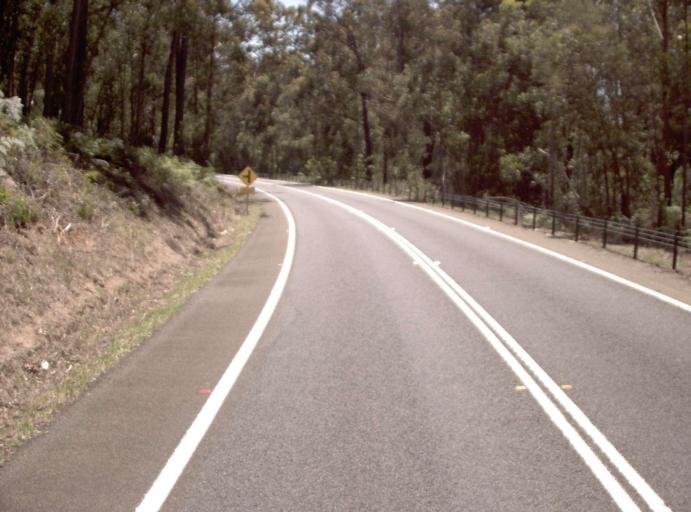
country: AU
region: Victoria
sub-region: East Gippsland
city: Lakes Entrance
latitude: -37.7845
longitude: 148.0542
